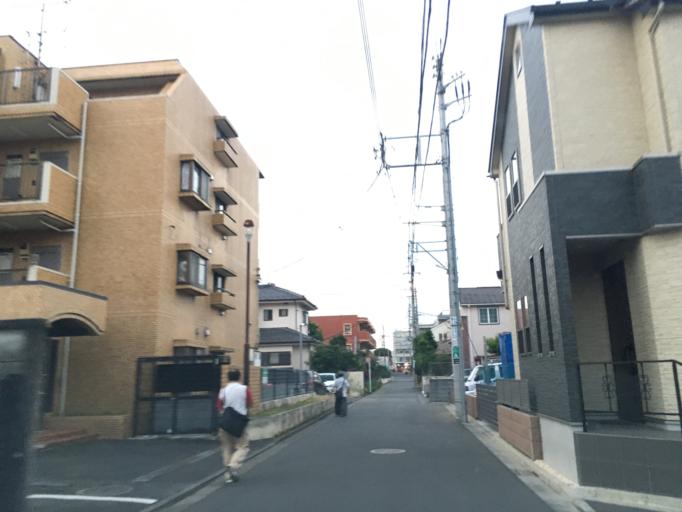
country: JP
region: Tokyo
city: Higashimurayama-shi
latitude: 35.7320
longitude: 139.4704
